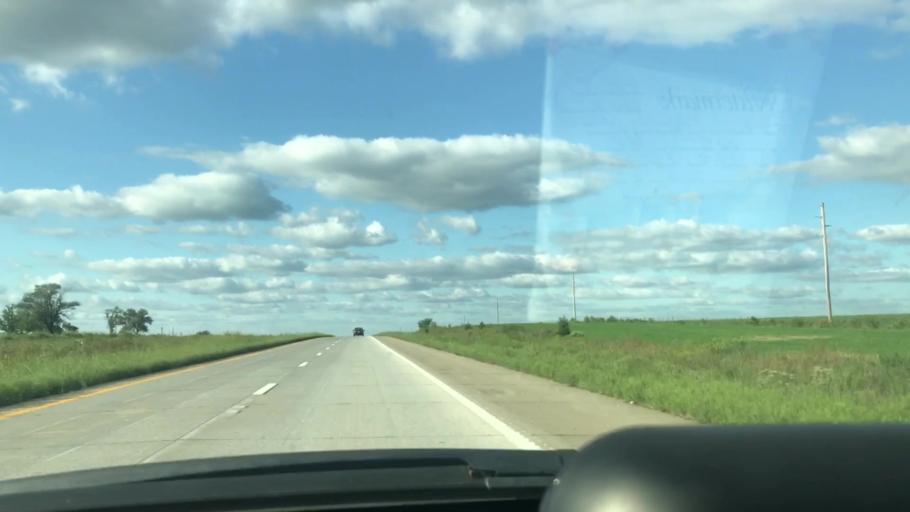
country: US
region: Missouri
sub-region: Benton County
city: Cole Camp
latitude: 38.5004
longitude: -93.2732
